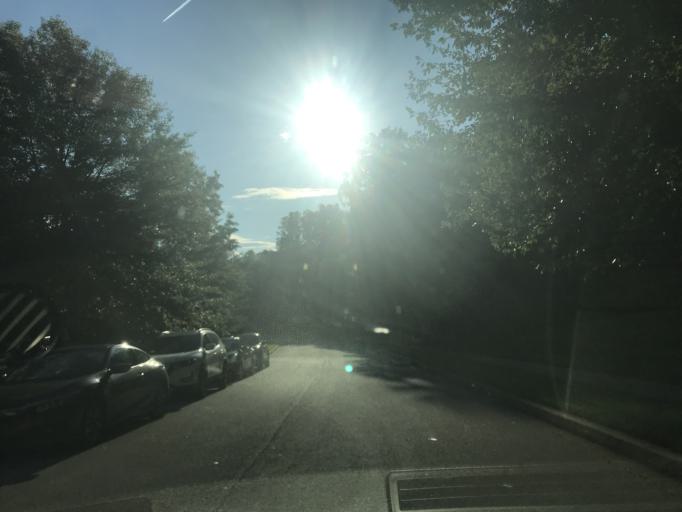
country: US
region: Maryland
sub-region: Harford County
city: South Bel Air
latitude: 39.5658
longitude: -76.3249
